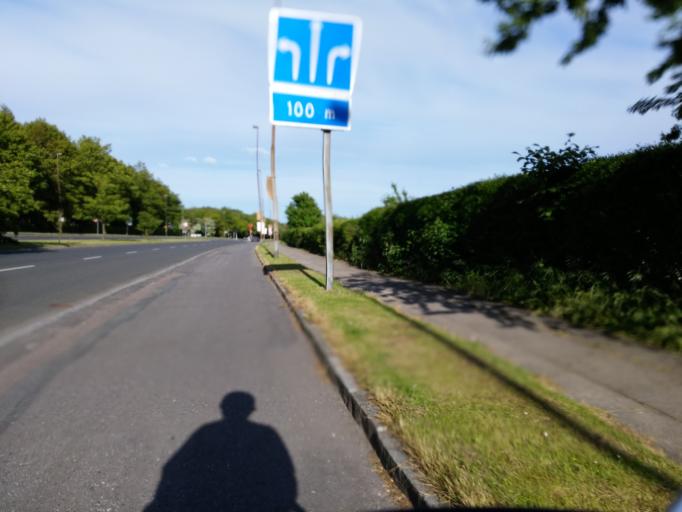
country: DK
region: South Denmark
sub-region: Odense Kommune
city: Seden
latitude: 55.4021
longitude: 10.4393
